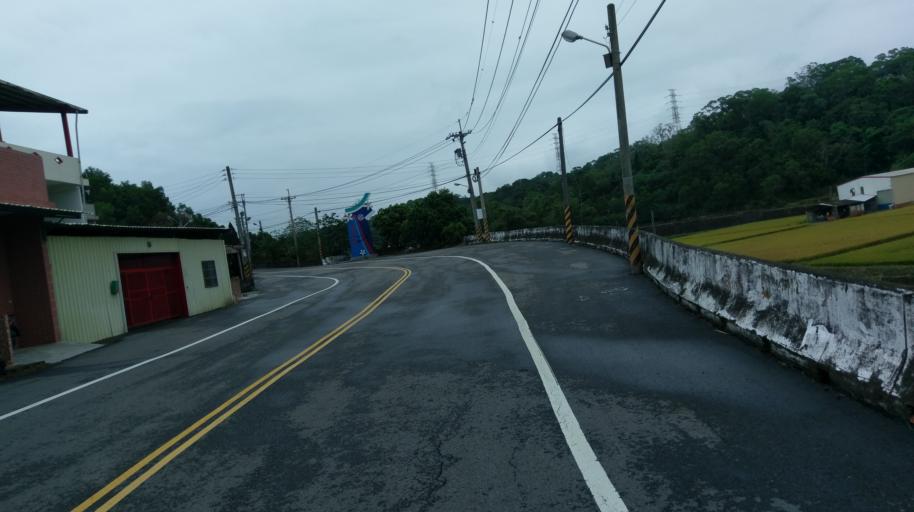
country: TW
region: Taiwan
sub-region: Hsinchu
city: Hsinchu
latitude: 24.7324
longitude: 120.9443
